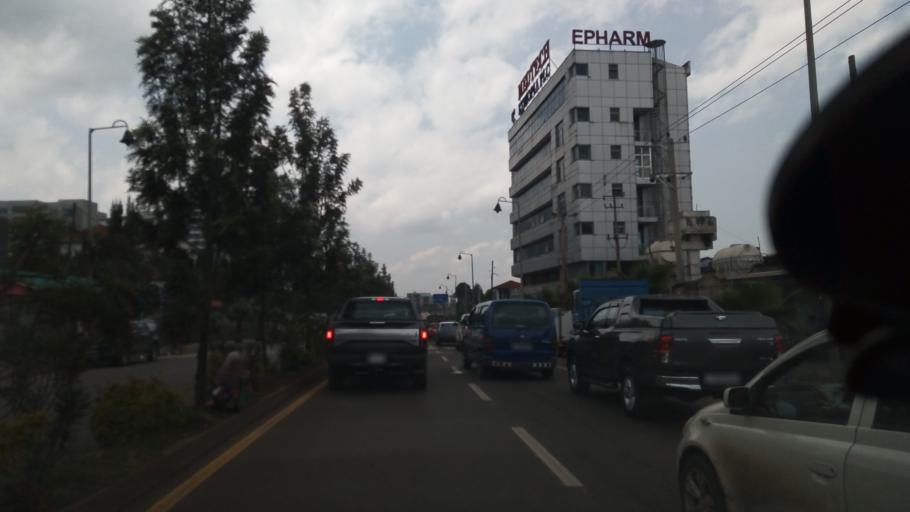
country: ET
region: Adis Abeba
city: Addis Ababa
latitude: 8.9898
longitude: 38.7215
